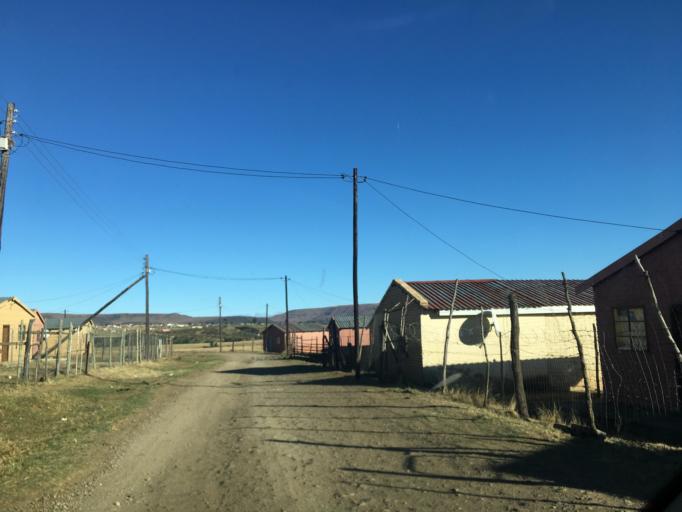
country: ZA
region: Eastern Cape
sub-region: Chris Hani District Municipality
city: Cala
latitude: -31.5380
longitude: 27.6808
